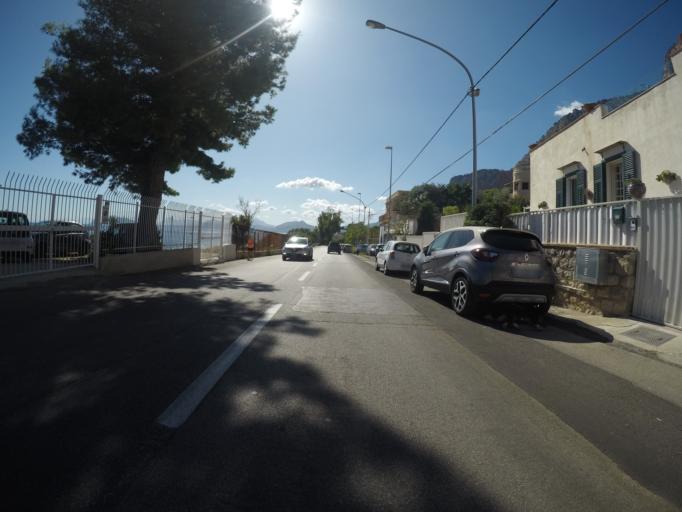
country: IT
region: Sicily
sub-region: Palermo
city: Palermo
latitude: 38.1718
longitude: 13.3662
